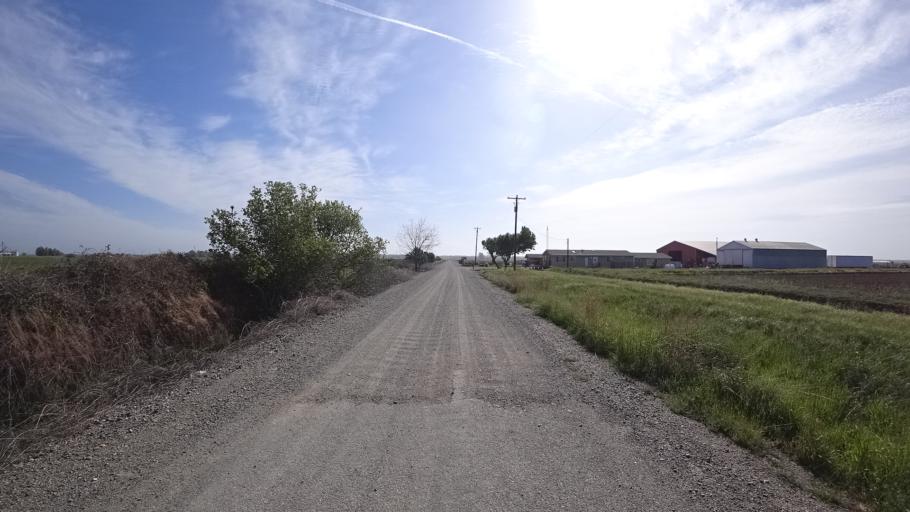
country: US
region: California
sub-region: Glenn County
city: Willows
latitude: 39.5726
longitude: -122.0354
